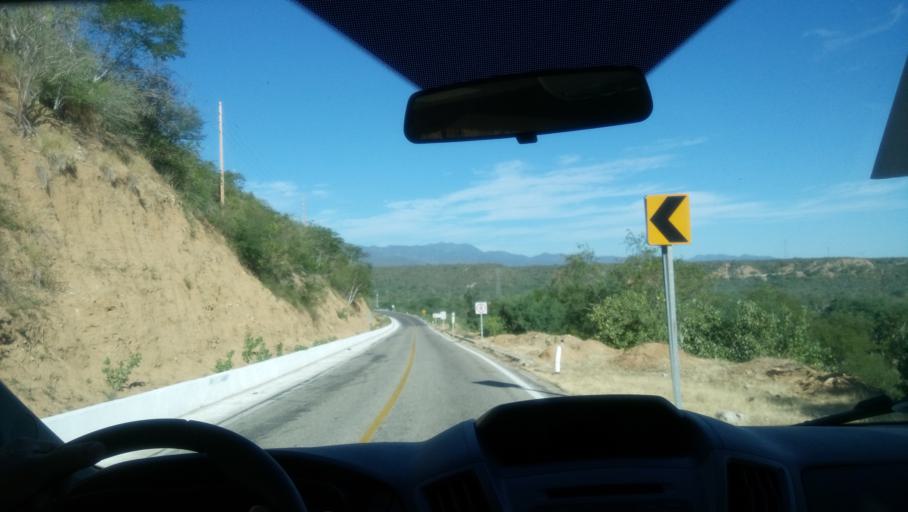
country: MX
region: Baja California Sur
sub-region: Los Cabos
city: Las Veredas
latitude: 23.3287
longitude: -109.7630
